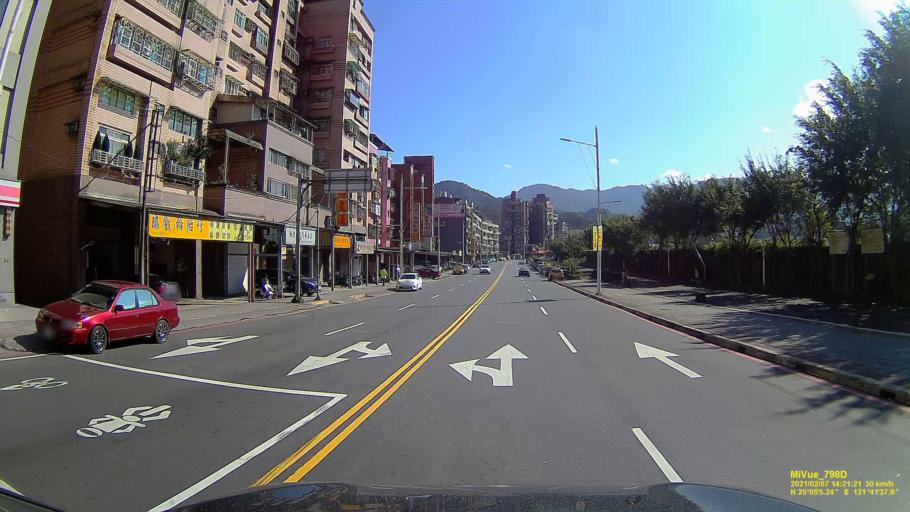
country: TW
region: Taiwan
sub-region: Keelung
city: Keelung
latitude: 25.0847
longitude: 121.6939
